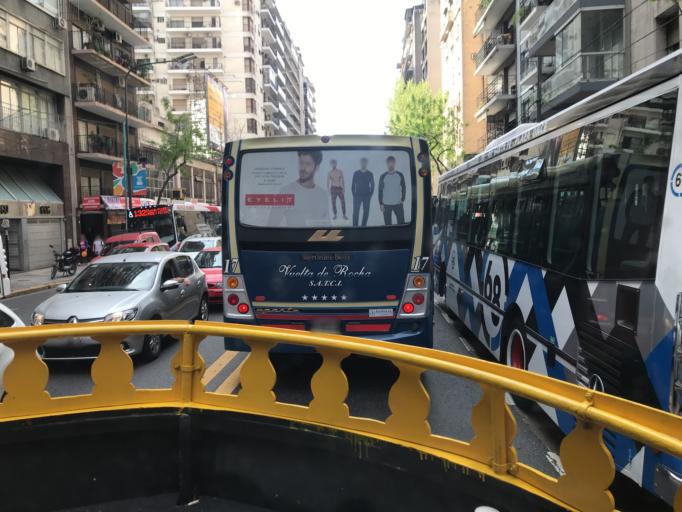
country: AR
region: Buenos Aires F.D.
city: Retiro
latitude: -34.6005
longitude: -58.4044
